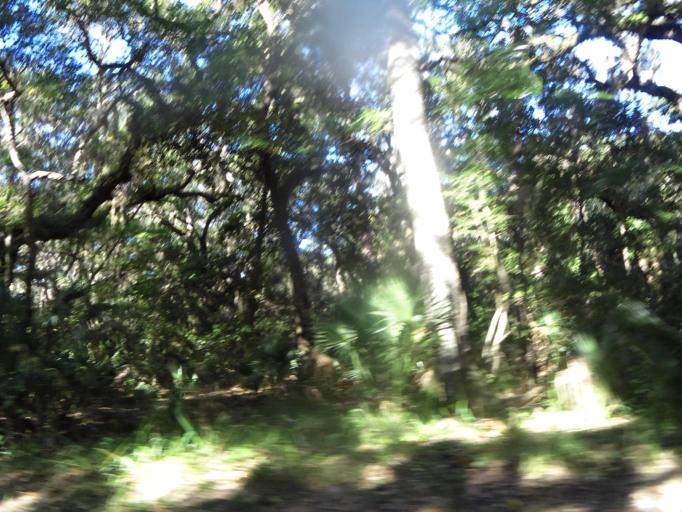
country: US
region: Florida
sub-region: Duval County
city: Atlantic Beach
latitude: 30.4356
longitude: -81.4326
